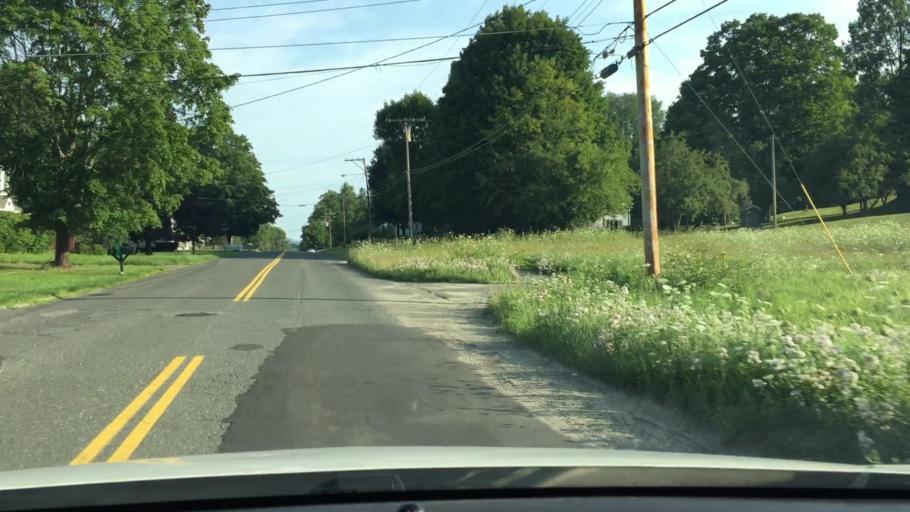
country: US
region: Massachusetts
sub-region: Berkshire County
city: Lee
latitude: 42.3109
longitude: -73.2325
